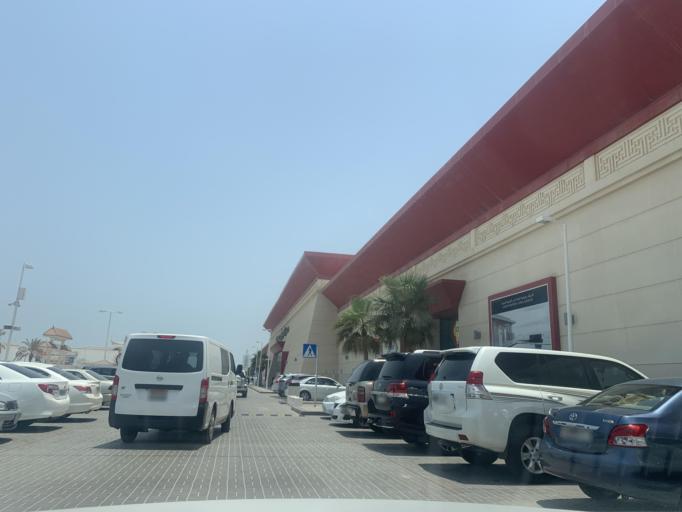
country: BH
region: Muharraq
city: Al Muharraq
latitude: 26.3067
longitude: 50.6243
